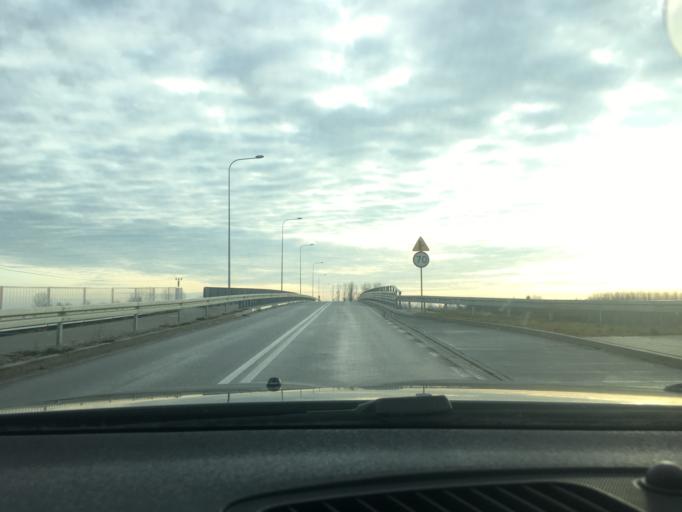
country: PL
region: Swietokrzyskie
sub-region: Powiat jedrzejowski
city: Jedrzejow
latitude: 50.6605
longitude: 20.3295
